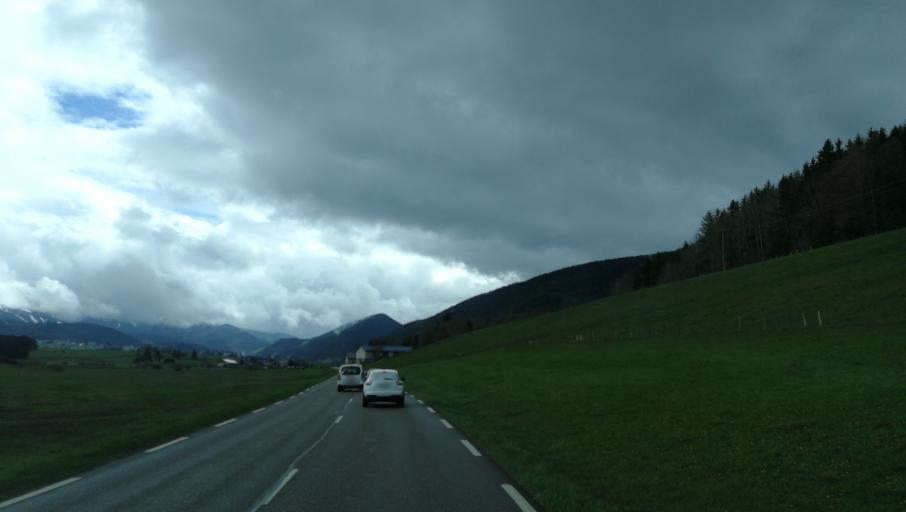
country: FR
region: Rhone-Alpes
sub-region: Departement de l'Isere
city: Lans-en-Vercors
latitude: 45.1069
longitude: 5.5637
